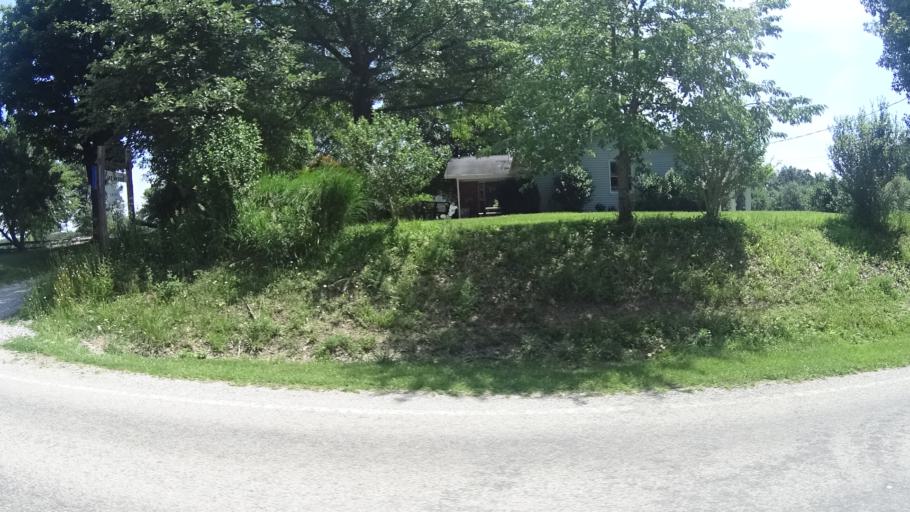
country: US
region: Ohio
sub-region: Erie County
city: Huron
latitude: 41.3397
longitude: -82.5093
